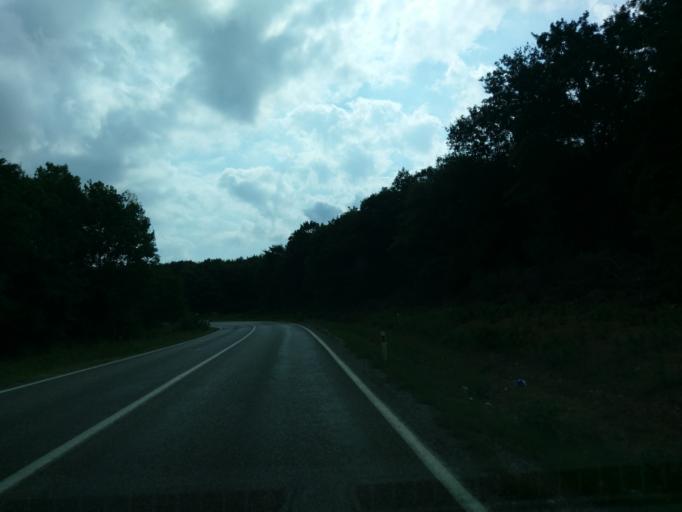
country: TR
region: Sinop
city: Yenikonak
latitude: 41.9445
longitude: 34.7386
